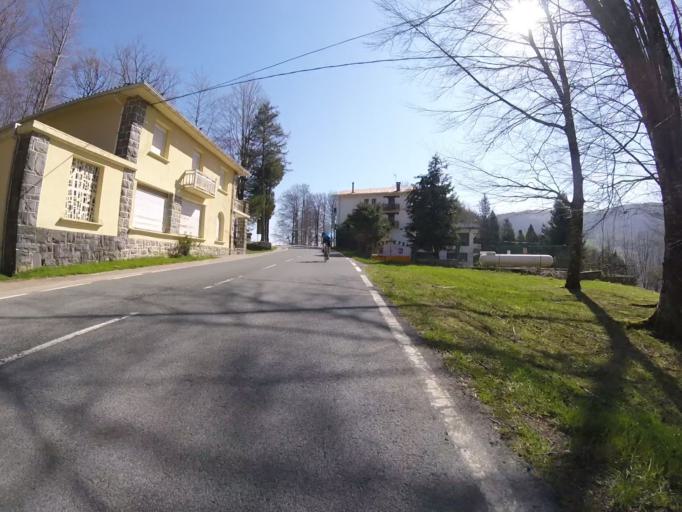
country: ES
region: Navarre
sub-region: Provincia de Navarra
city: Leitza
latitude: 43.0857
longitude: -1.8813
